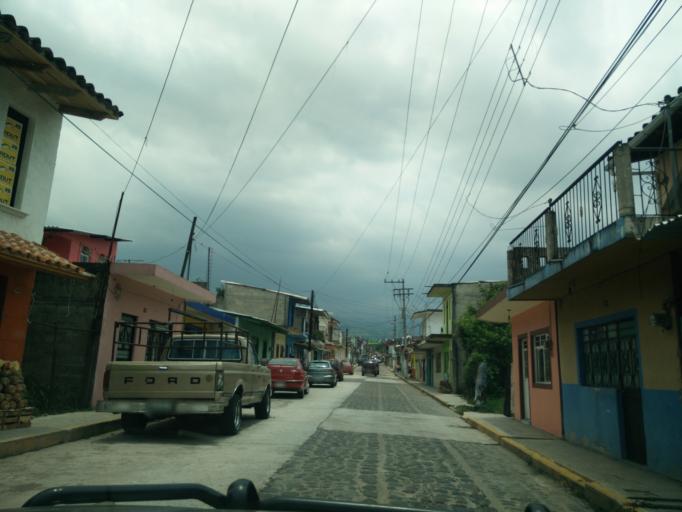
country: MX
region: Veracruz
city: Xico
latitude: 19.4213
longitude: -97.0020
